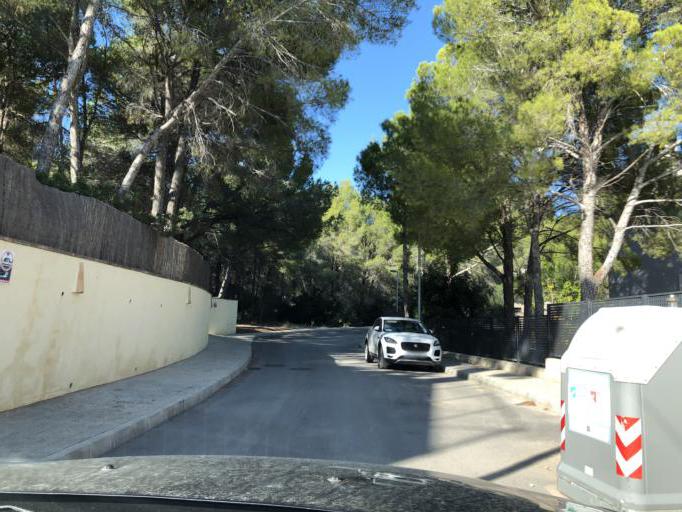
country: ES
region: Balearic Islands
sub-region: Illes Balears
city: Camp de Mar
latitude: 39.5413
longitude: 2.4139
